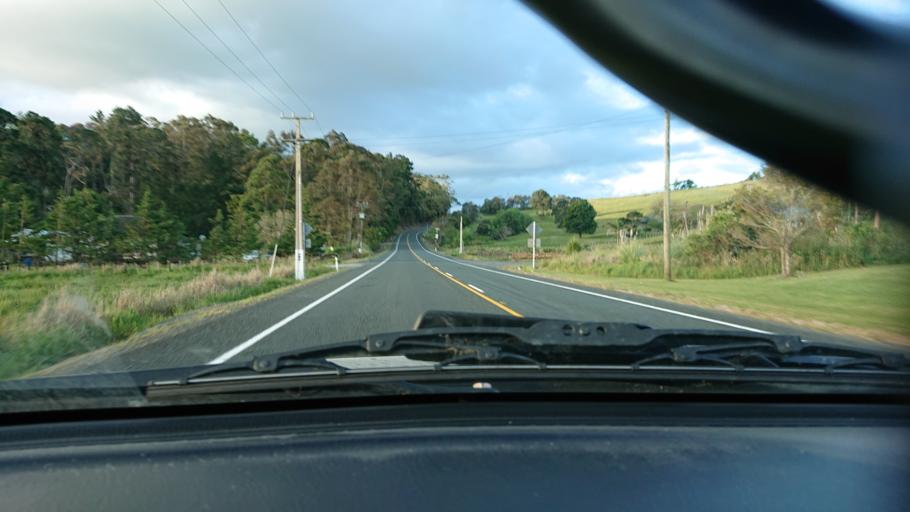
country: NZ
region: Auckland
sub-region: Auckland
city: Parakai
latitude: -36.5294
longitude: 174.4544
